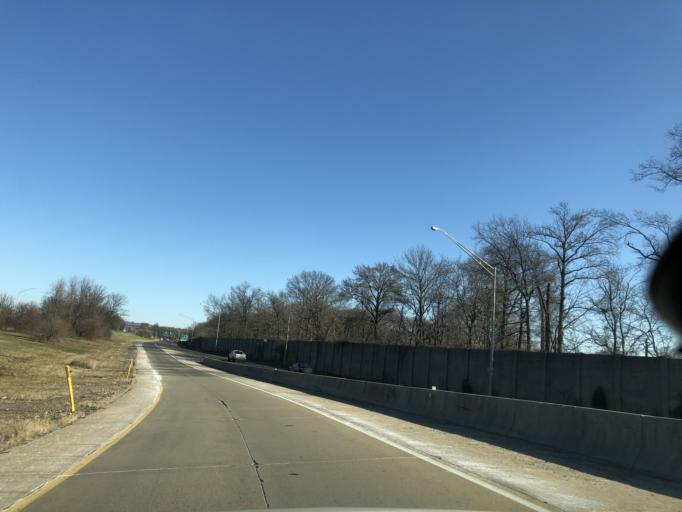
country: US
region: Pennsylvania
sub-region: Bucks County
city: Croydon
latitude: 40.1098
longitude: -74.8901
